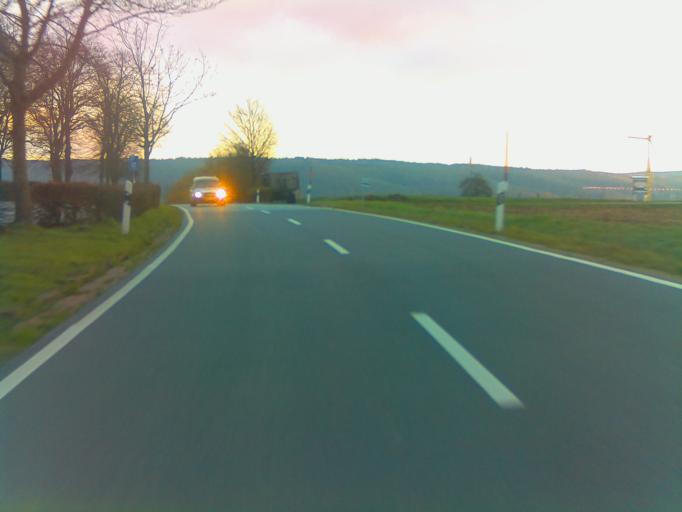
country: DE
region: Hesse
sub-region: Regierungsbezirk Darmstadt
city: Beerfelden
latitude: 49.5722
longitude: 8.9631
